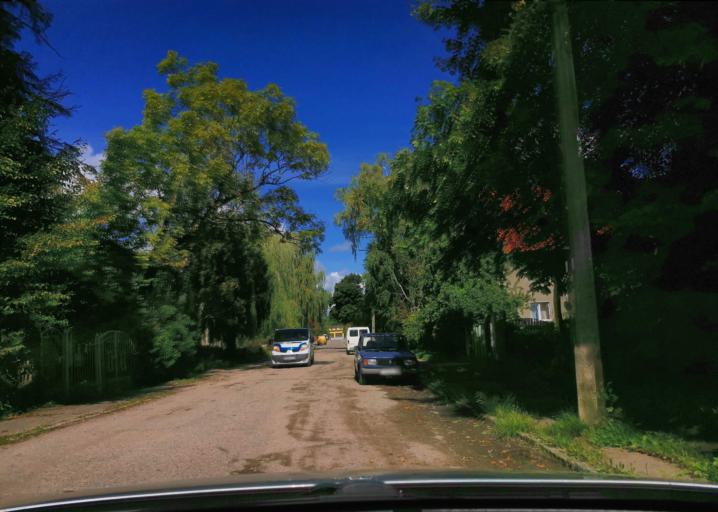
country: RU
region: Kaliningrad
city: Chernyakhovsk
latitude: 54.6355
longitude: 21.8404
